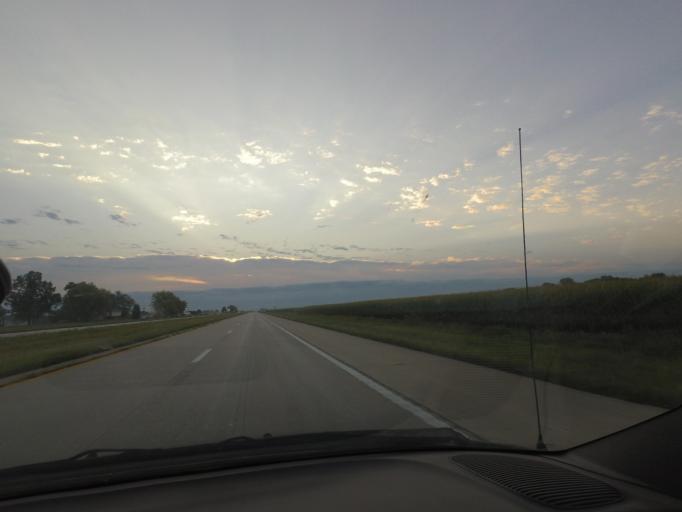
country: US
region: Missouri
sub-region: Macon County
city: Macon
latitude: 39.7501
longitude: -92.3382
